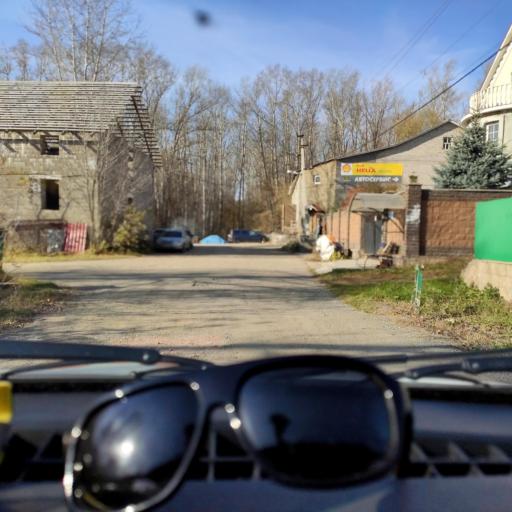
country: RU
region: Bashkortostan
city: Ufa
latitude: 54.7040
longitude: 55.9409
